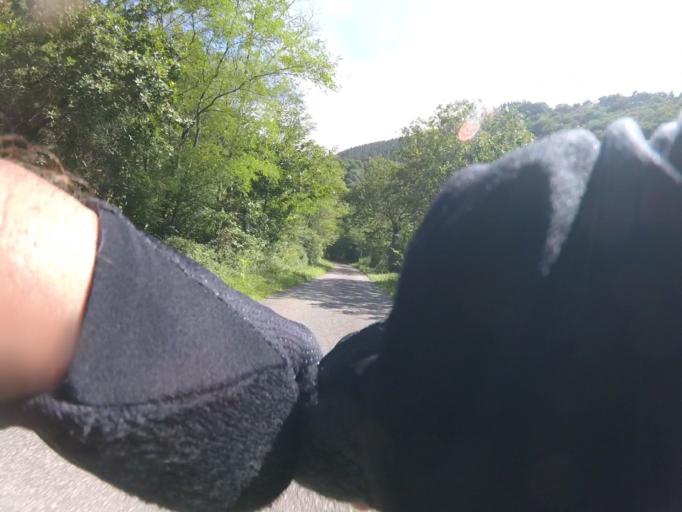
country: ES
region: Navarre
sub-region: Provincia de Navarra
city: Igantzi
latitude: 43.2215
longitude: -1.6778
